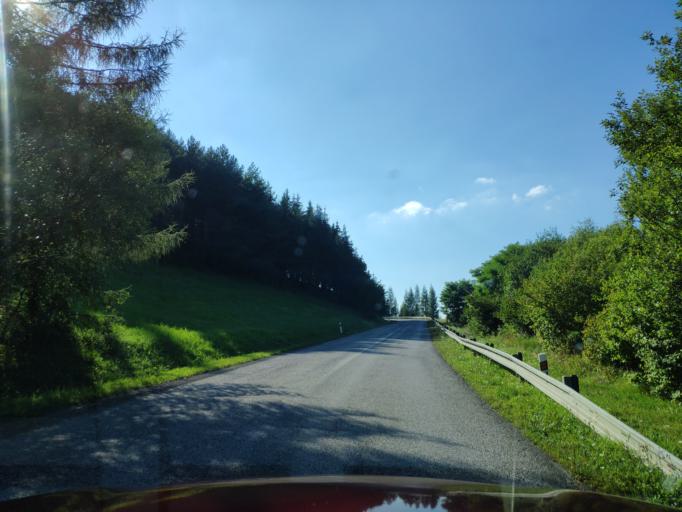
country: SK
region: Presovsky
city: Snina
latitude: 49.0518
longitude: 22.3006
